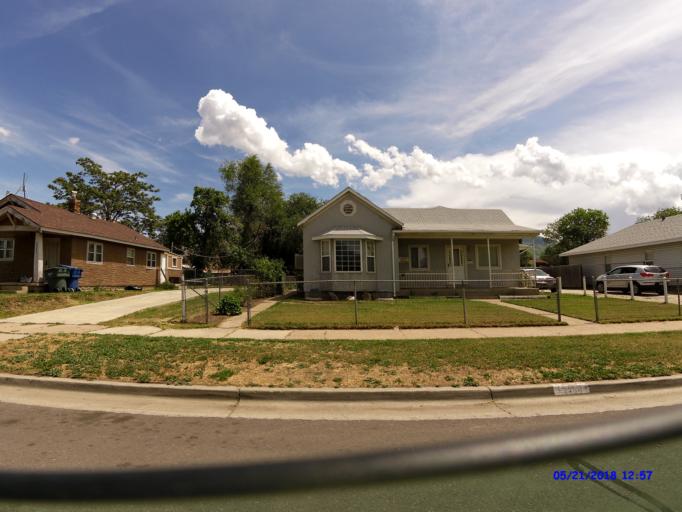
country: US
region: Utah
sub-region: Weber County
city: South Ogden
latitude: 41.2044
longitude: -111.9764
